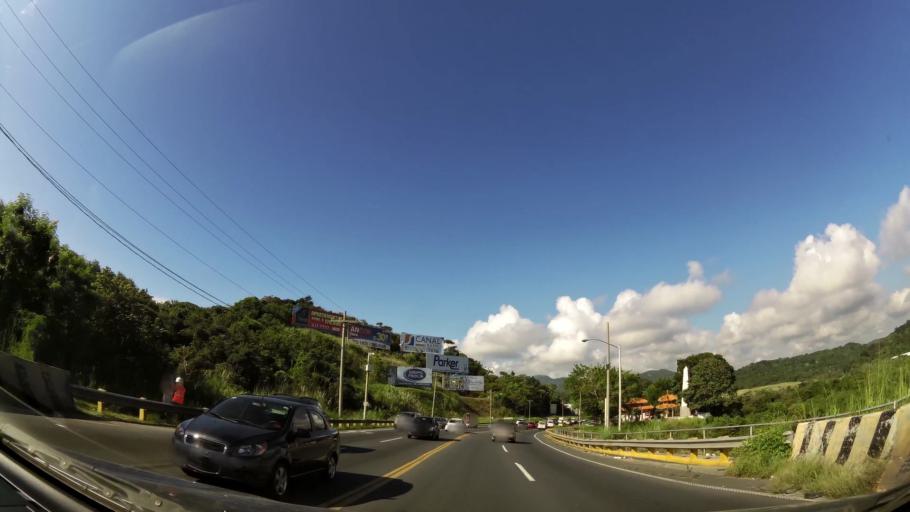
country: PA
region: Panama
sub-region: Distrito de Panama
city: Ancon
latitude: 8.9407
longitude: -79.5711
